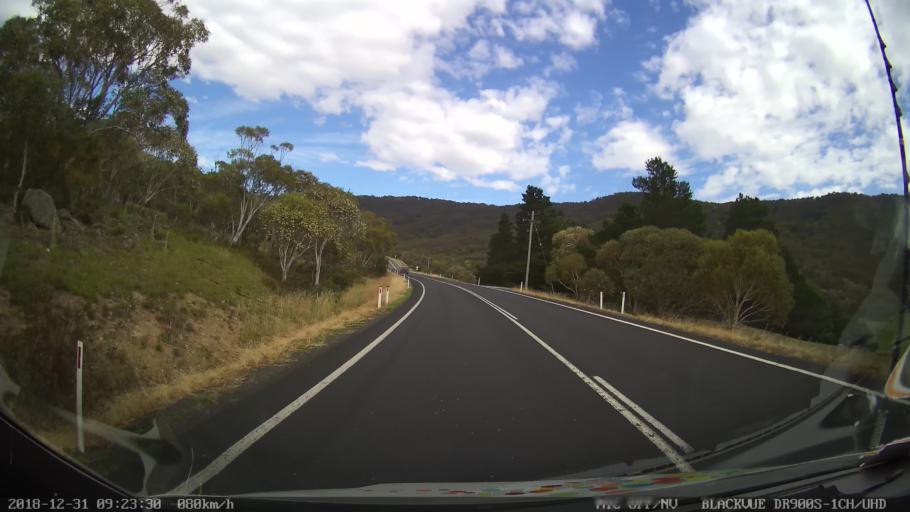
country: AU
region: New South Wales
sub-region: Snowy River
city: Jindabyne
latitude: -36.4365
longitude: 148.5333
